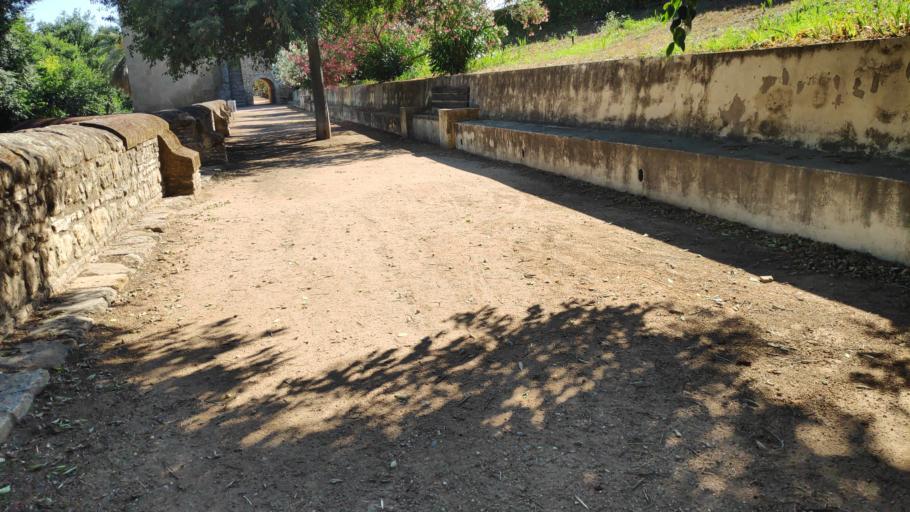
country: ES
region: Andalusia
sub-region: Province of Cordoba
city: Cordoba
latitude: 37.8745
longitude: -4.7825
